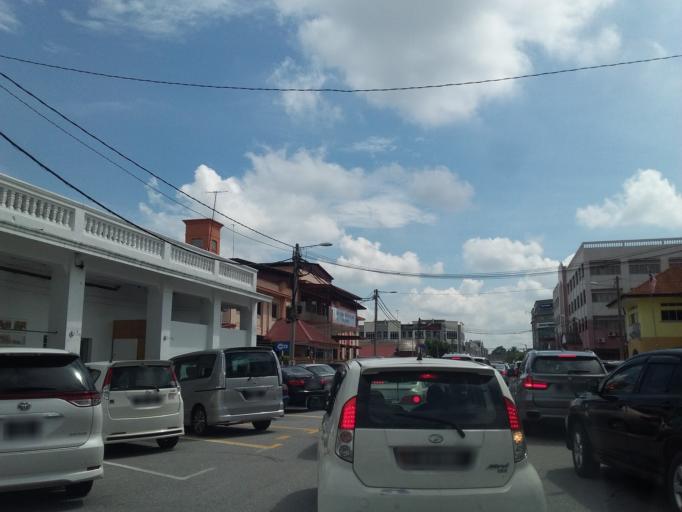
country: MY
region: Johor
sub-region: Daerah Batu Pahat
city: Batu Pahat
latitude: 1.8493
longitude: 102.9299
